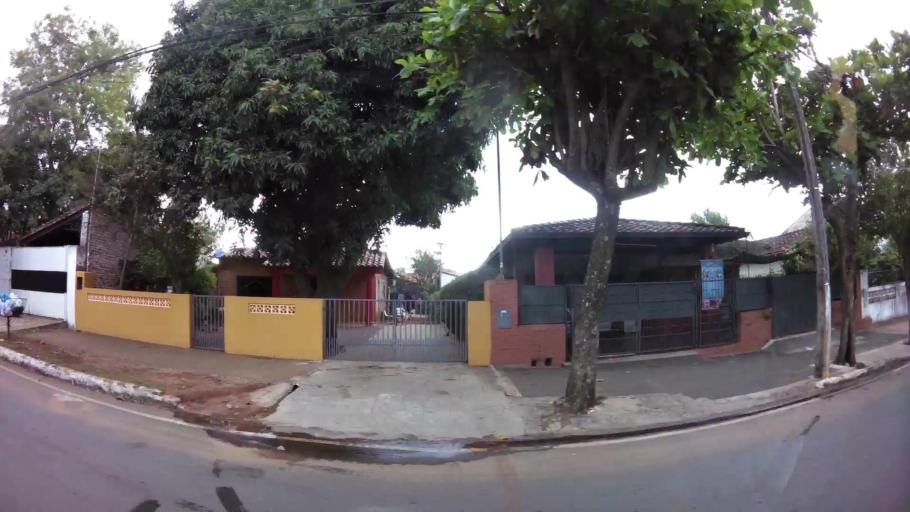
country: PY
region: Central
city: Fernando de la Mora
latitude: -25.3282
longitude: -57.5533
